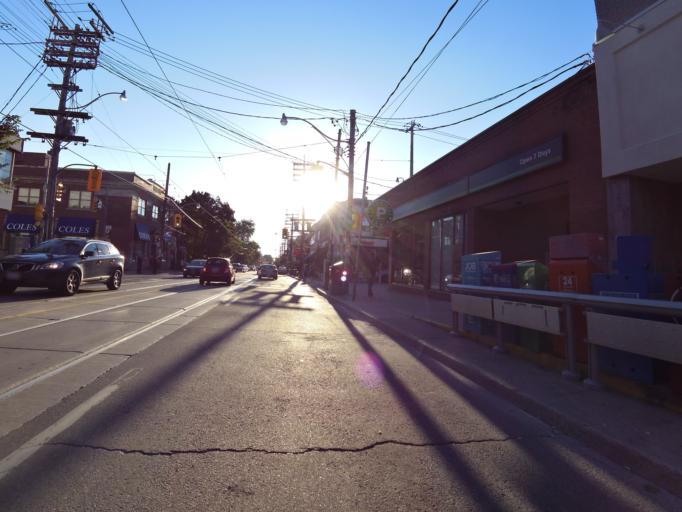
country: CA
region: Ontario
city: Scarborough
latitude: 43.6706
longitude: -79.2976
